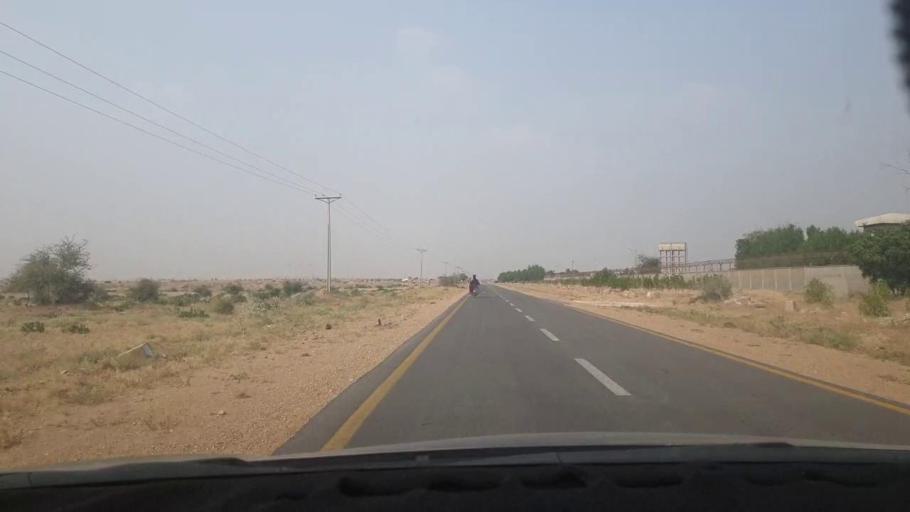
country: PK
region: Sindh
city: Jamshoro
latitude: 25.5575
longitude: 68.3194
